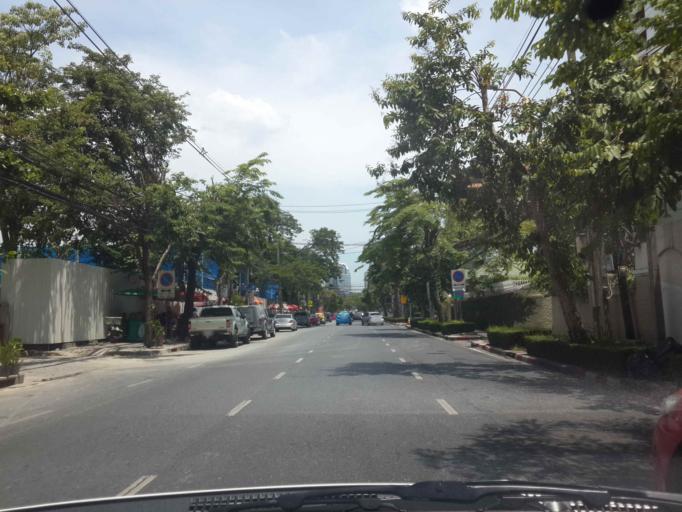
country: TH
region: Bangkok
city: Pathum Wan
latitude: 13.7377
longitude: 100.5427
